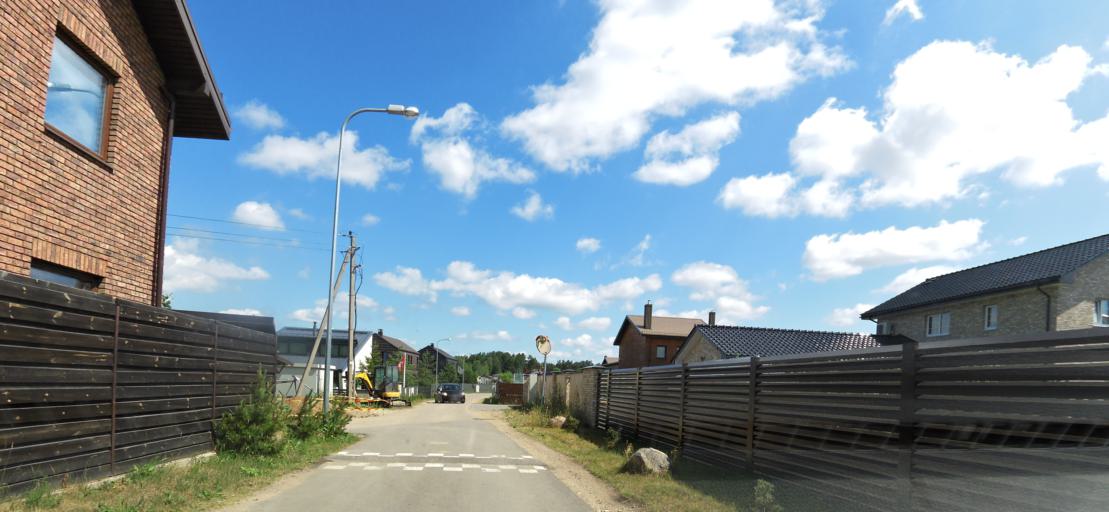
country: LT
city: Nemencine
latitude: 54.8204
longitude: 25.3943
